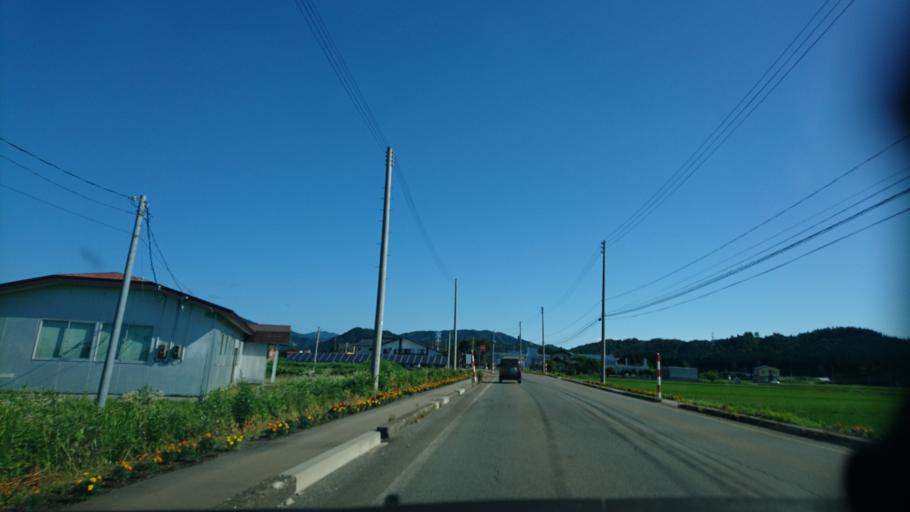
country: JP
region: Akita
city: Kakunodatemachi
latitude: 39.6531
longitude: 140.5709
